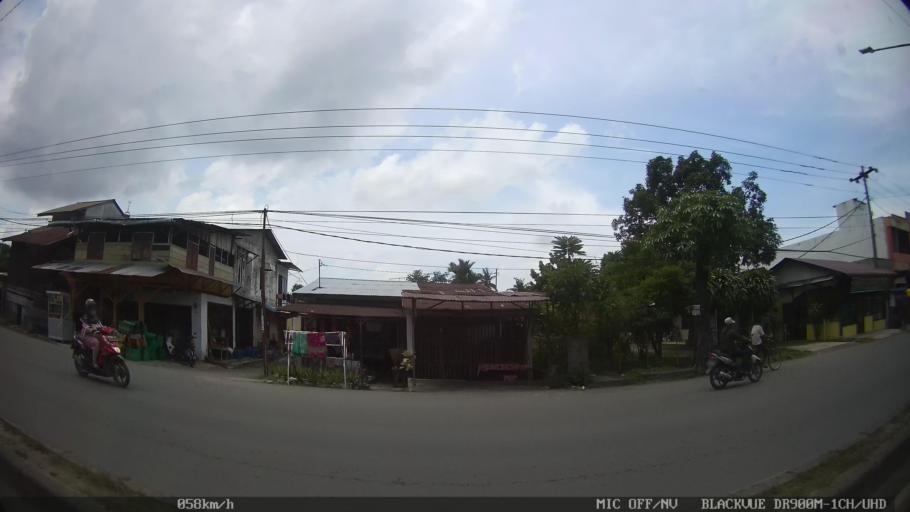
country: ID
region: North Sumatra
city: Labuhan Deli
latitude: 3.6992
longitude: 98.6752
